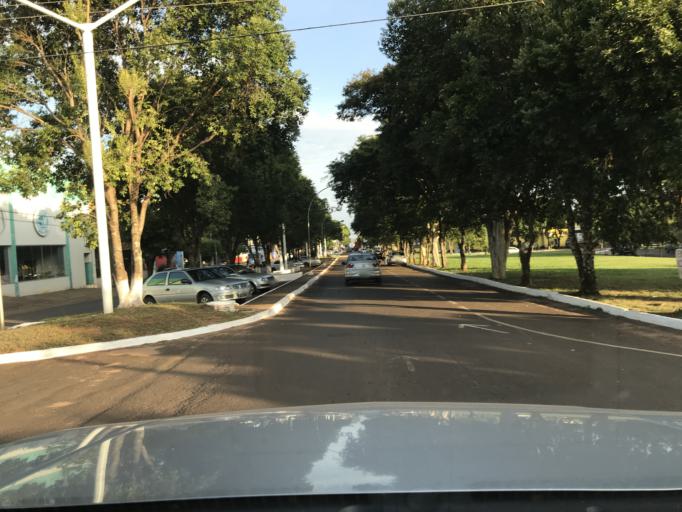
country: BR
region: Mato Grosso do Sul
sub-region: Iguatemi
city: Iguatemi
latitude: -23.6736
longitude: -54.5607
